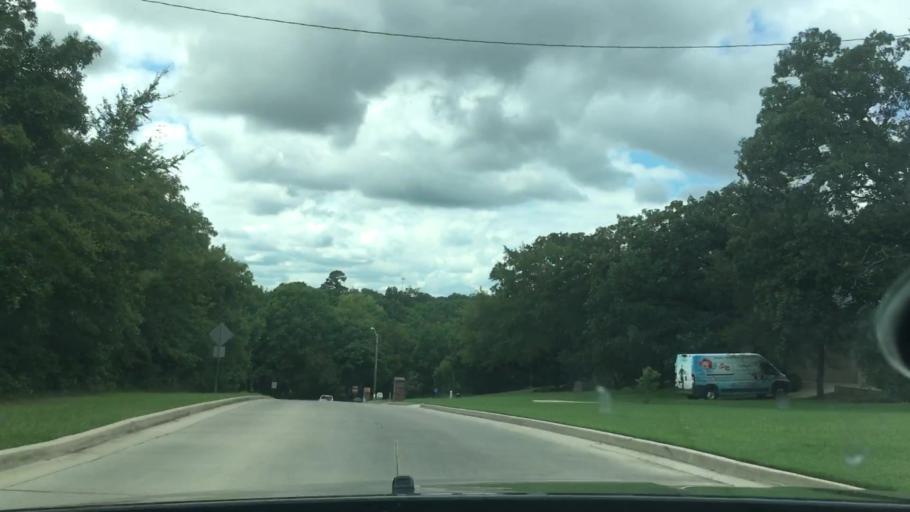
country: US
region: Oklahoma
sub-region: Pontotoc County
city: Ada
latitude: 34.7572
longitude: -96.6525
